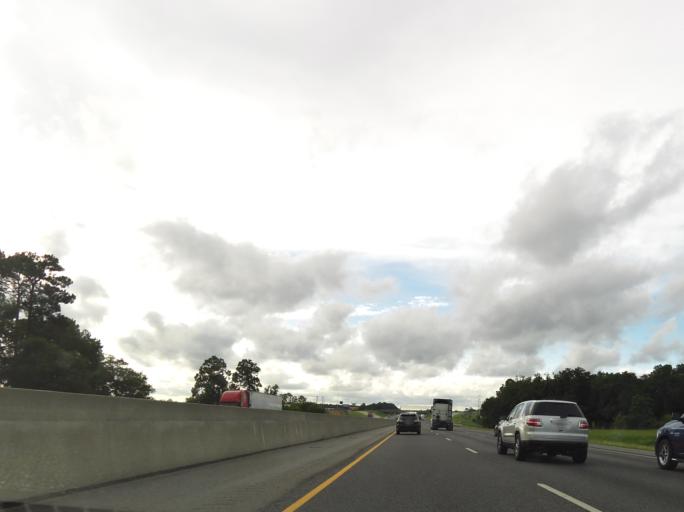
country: US
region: Georgia
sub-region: Turner County
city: Ashburn
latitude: 31.6216
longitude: -83.5723
